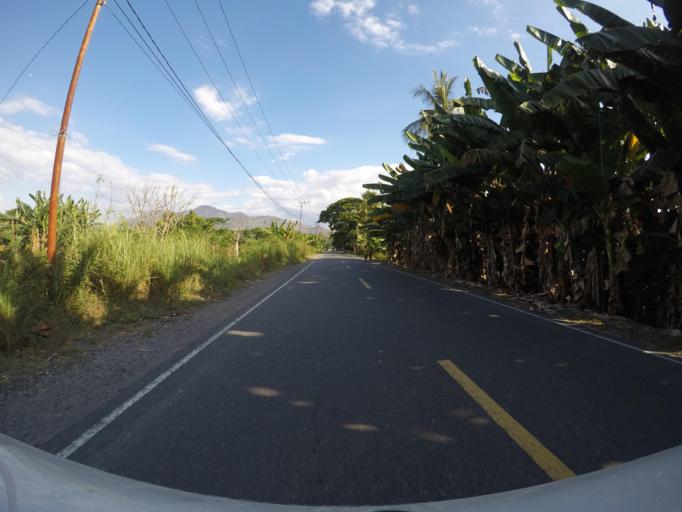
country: TL
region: Liquica
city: Maubara
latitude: -8.7349
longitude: 125.1364
